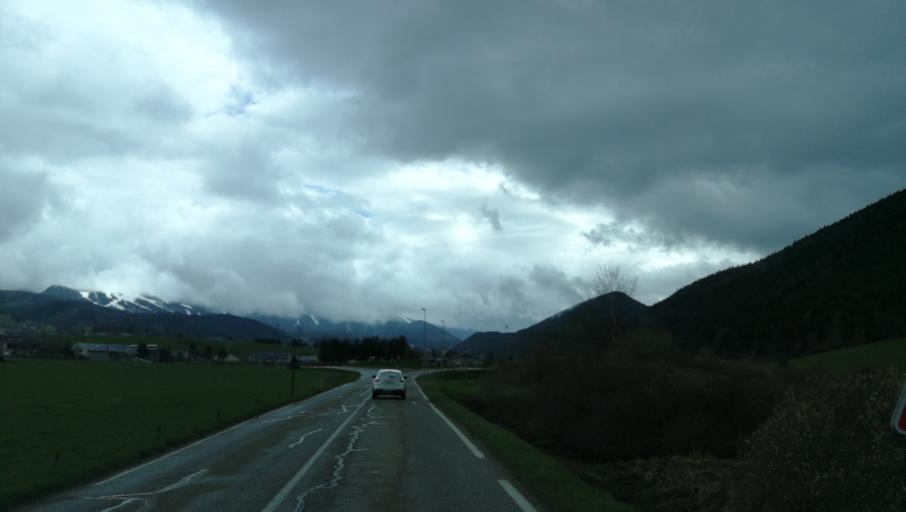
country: FR
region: Rhone-Alpes
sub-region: Departement de l'Isere
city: Villard-de-Lans
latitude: 45.0917
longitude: 5.5560
